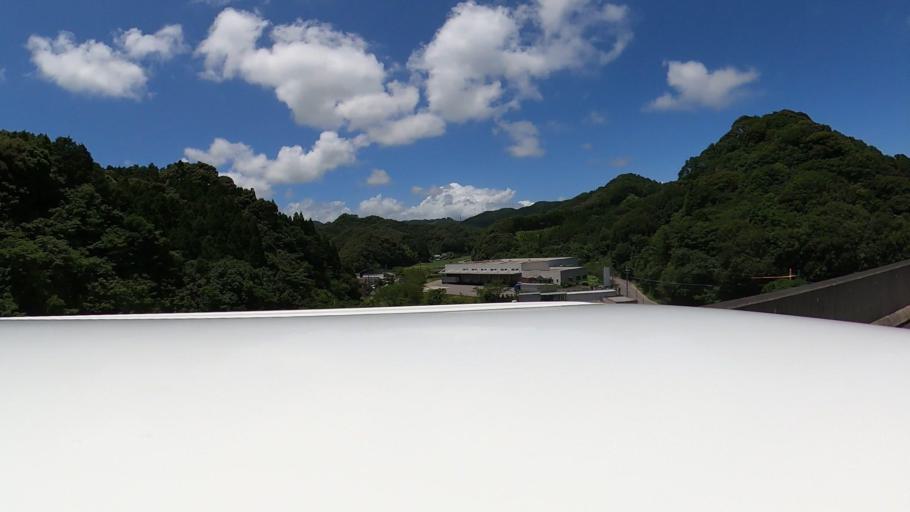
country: JP
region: Miyazaki
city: Nobeoka
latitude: 32.4982
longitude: 131.6605
